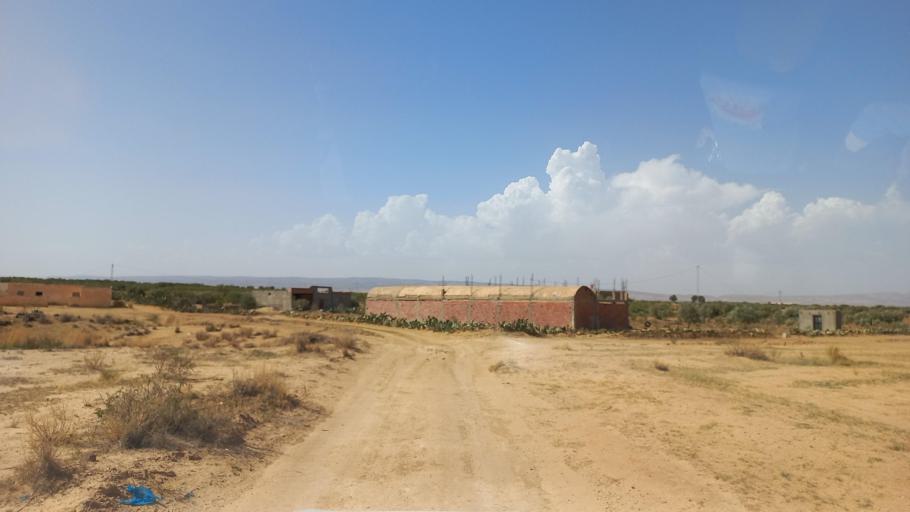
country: TN
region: Al Qasrayn
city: Kasserine
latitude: 35.2104
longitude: 9.0374
